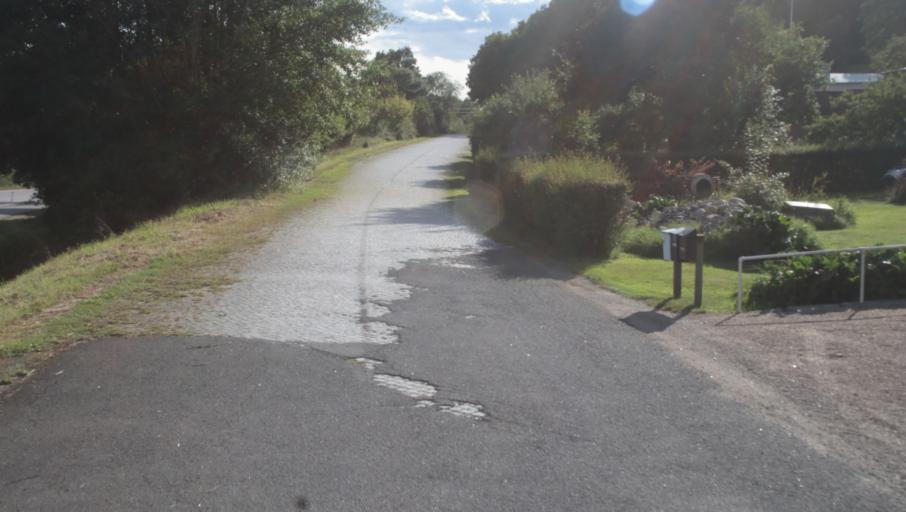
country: SE
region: Blekinge
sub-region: Karlshamns Kommun
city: Karlshamn
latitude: 56.1742
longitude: 14.9013
